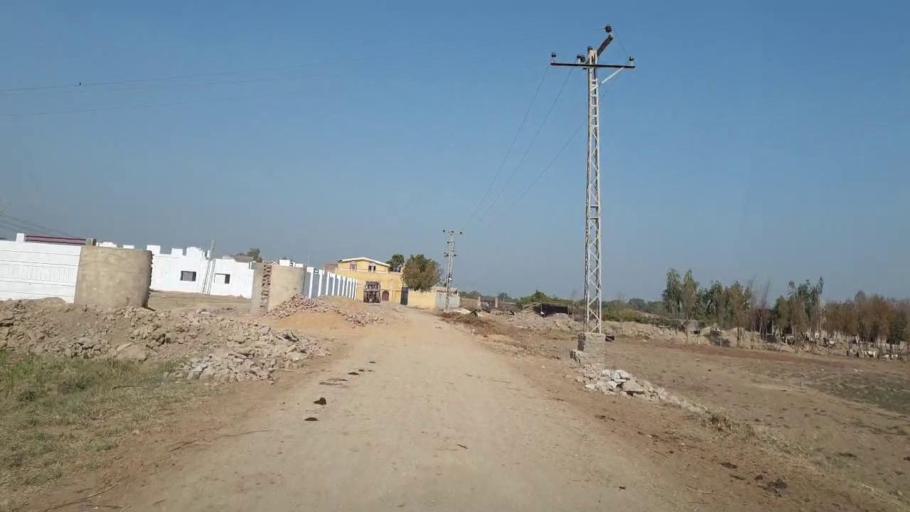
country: PK
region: Sindh
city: Matiari
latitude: 25.5066
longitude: 68.4593
